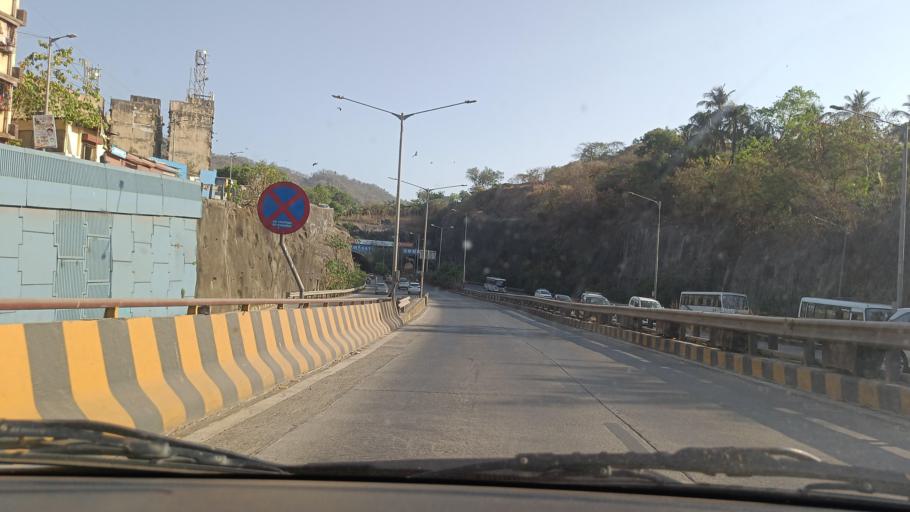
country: IN
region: Maharashtra
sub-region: Mumbai Suburban
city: Mumbai
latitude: 19.0415
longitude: 72.9087
